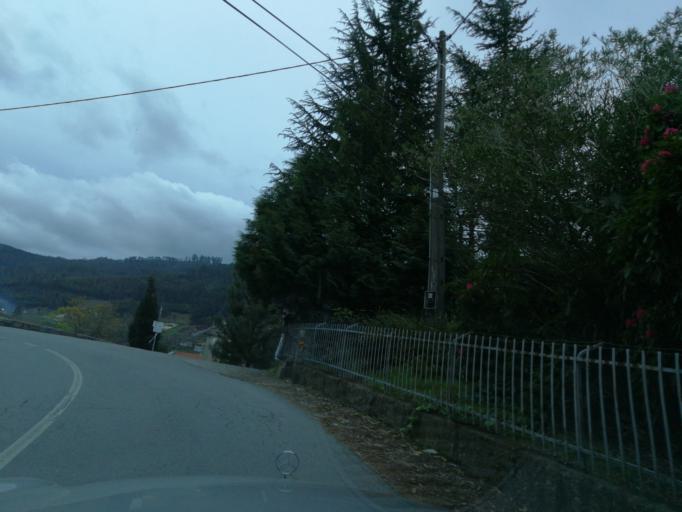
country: PT
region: Braga
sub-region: Braga
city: Oliveira
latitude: 41.4783
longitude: -8.4707
